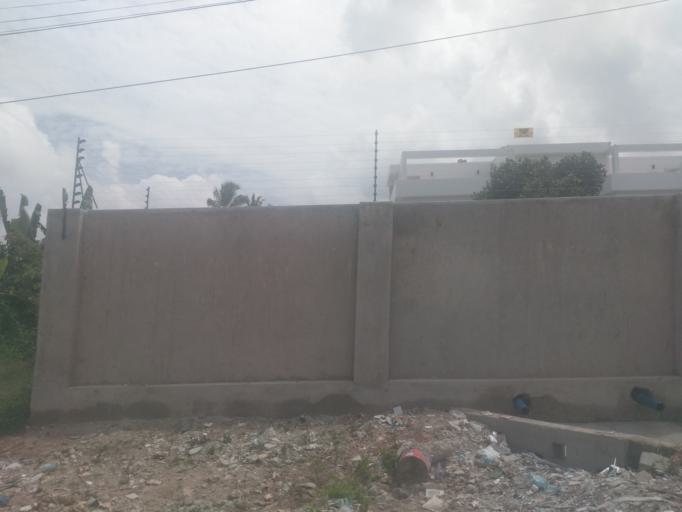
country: TZ
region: Zanzibar Urban/West
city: Zanzibar
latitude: -6.2373
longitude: 39.2137
